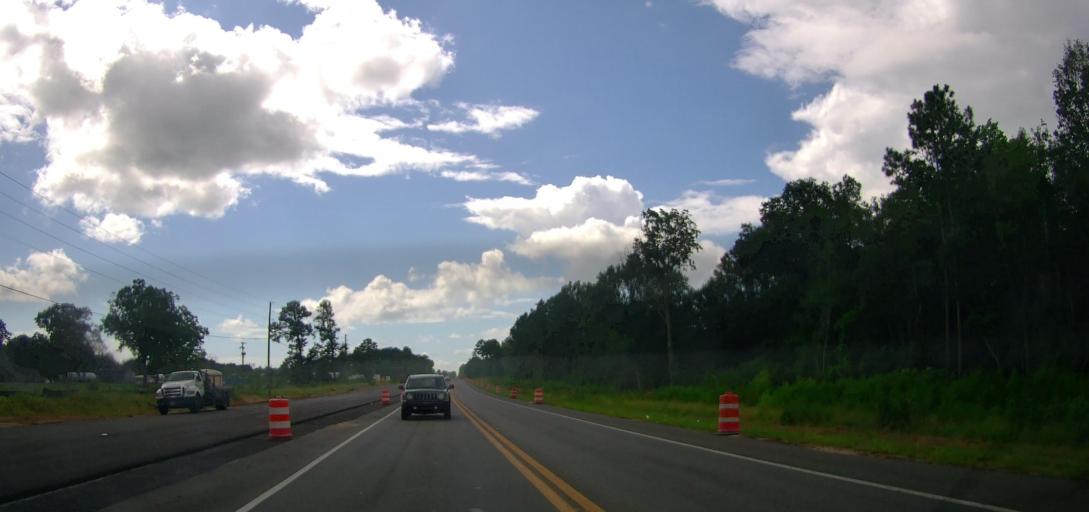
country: US
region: Georgia
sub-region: Coffee County
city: Douglas
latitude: 31.5224
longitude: -82.8955
